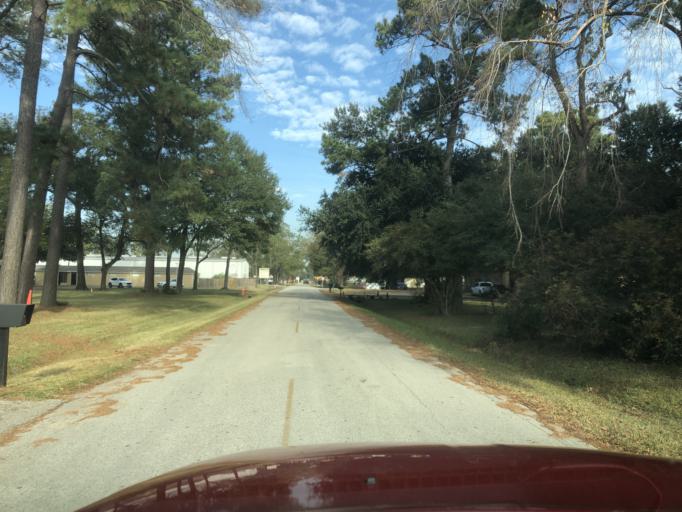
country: US
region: Texas
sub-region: Harris County
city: Hudson
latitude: 29.9960
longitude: -95.4746
